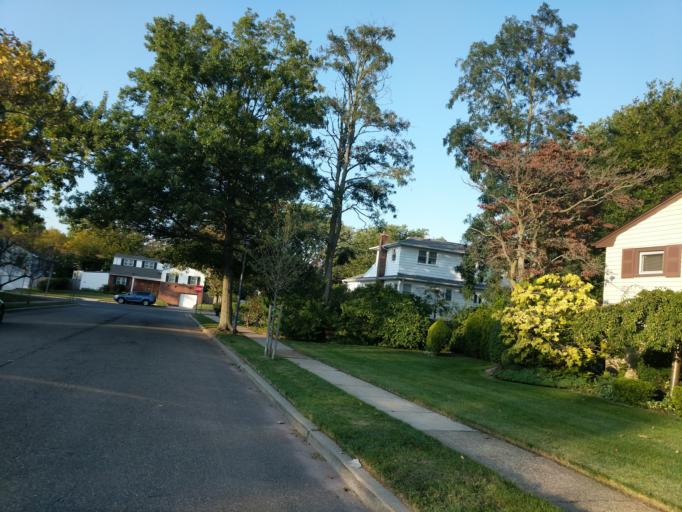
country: US
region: New York
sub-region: Nassau County
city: South Valley Stream
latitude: 40.6563
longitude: -73.7211
